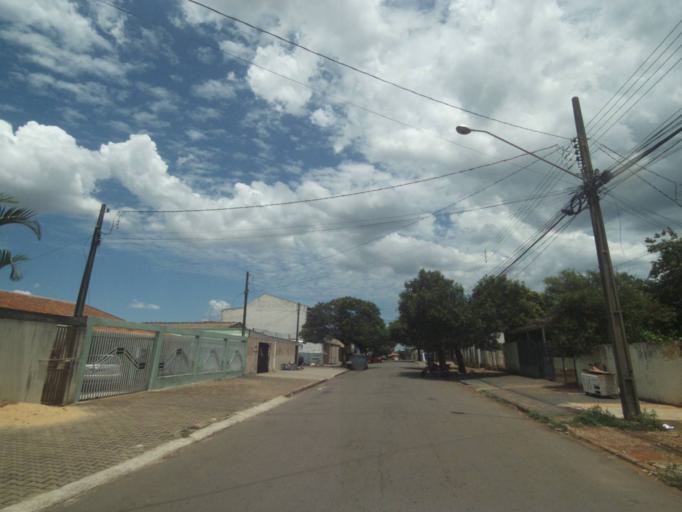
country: BR
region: Parana
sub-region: Londrina
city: Londrina
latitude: -23.3098
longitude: -51.2175
